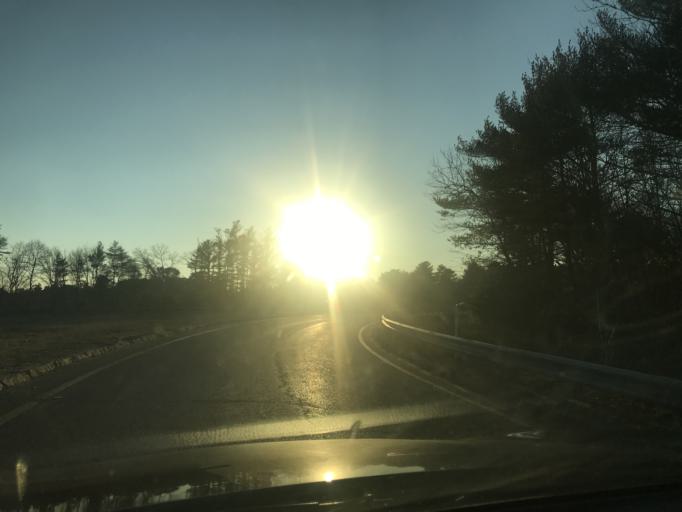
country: US
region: Massachusetts
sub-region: Plymouth County
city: Middleborough Center
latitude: 41.8466
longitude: -70.8474
